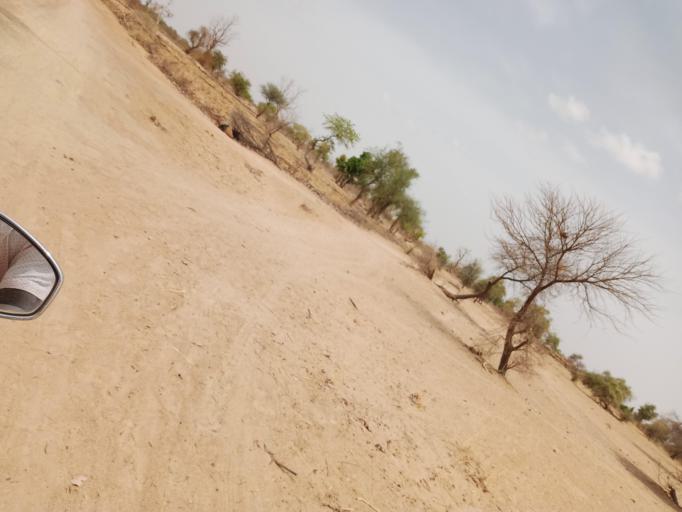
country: BF
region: Est
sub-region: Gnagna Province
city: Bogande
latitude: 13.0981
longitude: -0.0498
